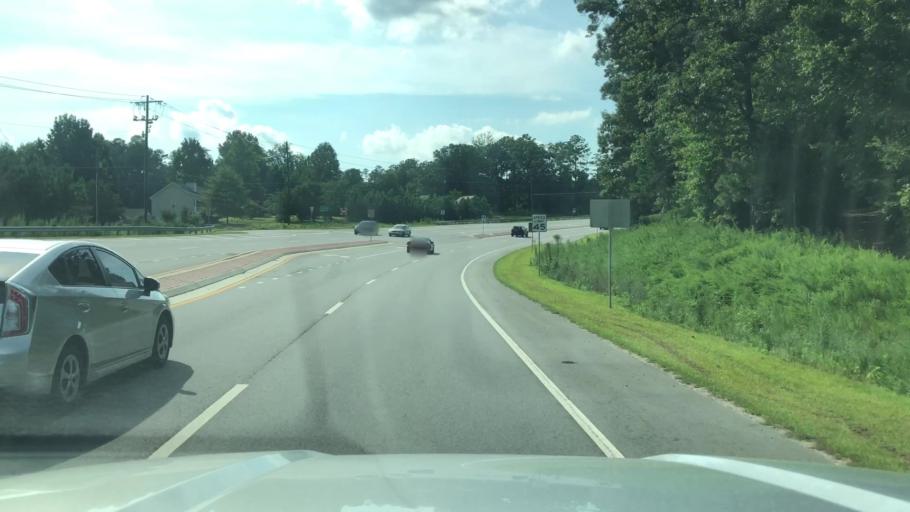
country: US
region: Georgia
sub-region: Paulding County
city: Hiram
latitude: 33.8616
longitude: -84.7792
